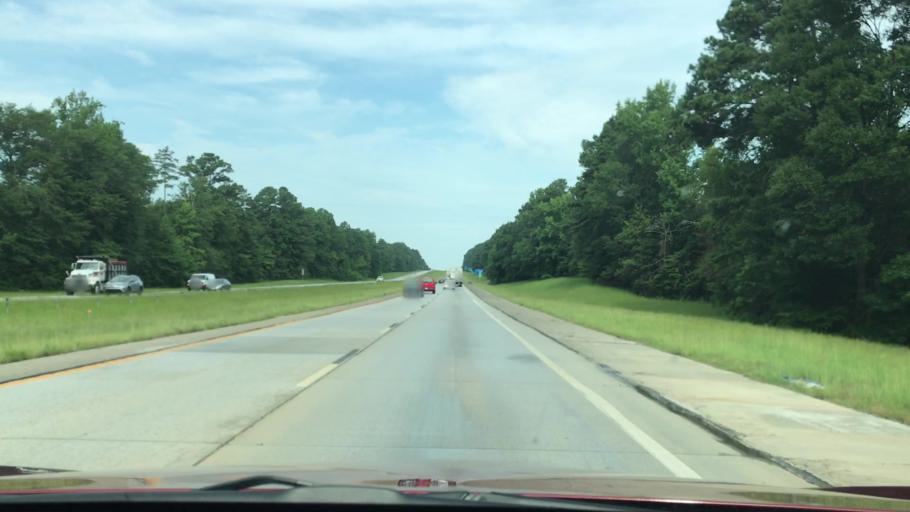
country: US
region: Georgia
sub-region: McDuffie County
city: Thomson
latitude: 33.5080
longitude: -82.4138
